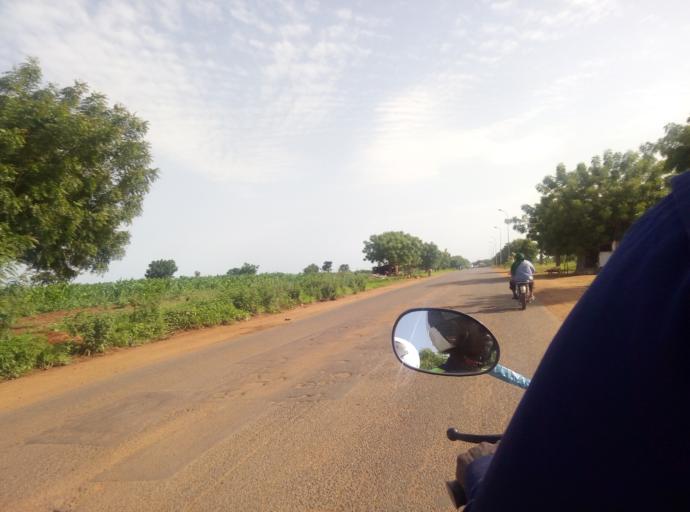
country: ML
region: Bamako
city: Bamako
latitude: 12.5530
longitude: -7.9484
